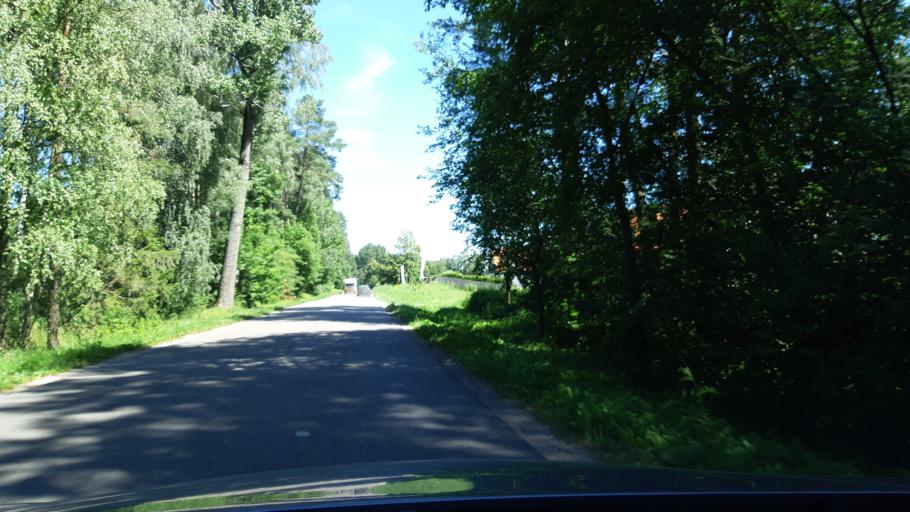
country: PL
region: Warmian-Masurian Voivodeship
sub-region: Powiat gizycki
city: Gizycko
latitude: 53.9721
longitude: 21.7927
